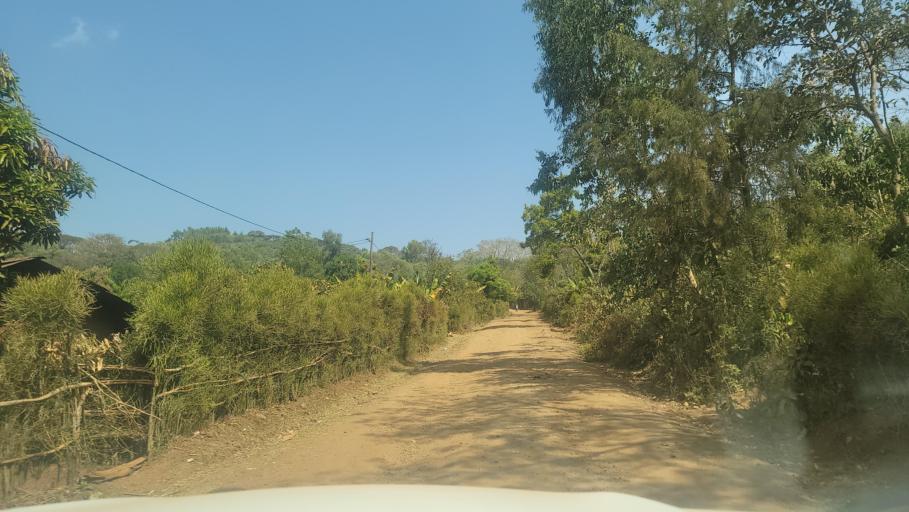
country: ET
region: Oromiya
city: Agaro
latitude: 7.8406
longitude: 36.5356
